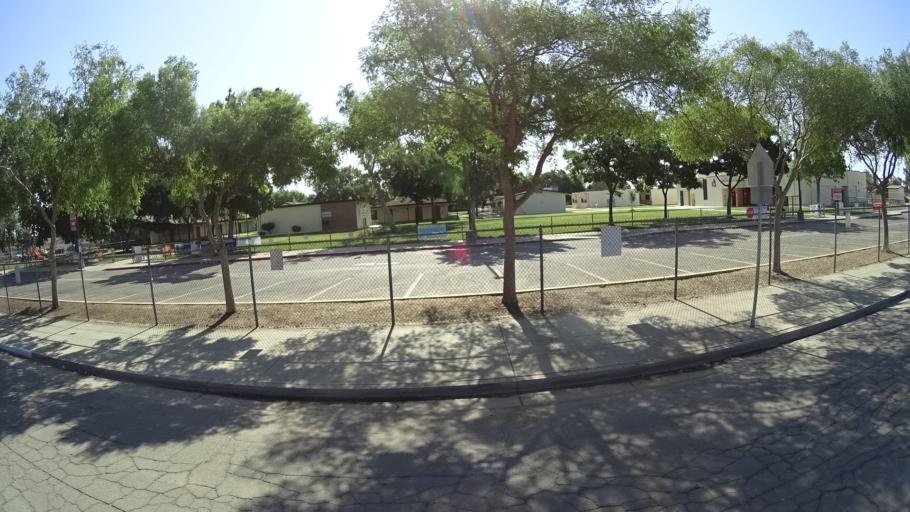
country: US
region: California
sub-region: Fresno County
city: West Park
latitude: 36.7242
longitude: -119.8312
